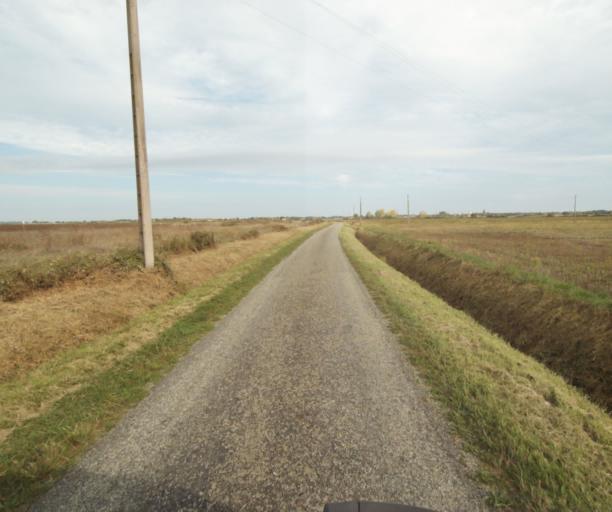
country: FR
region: Midi-Pyrenees
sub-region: Departement du Tarn-et-Garonne
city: Finhan
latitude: 43.9315
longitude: 1.2249
